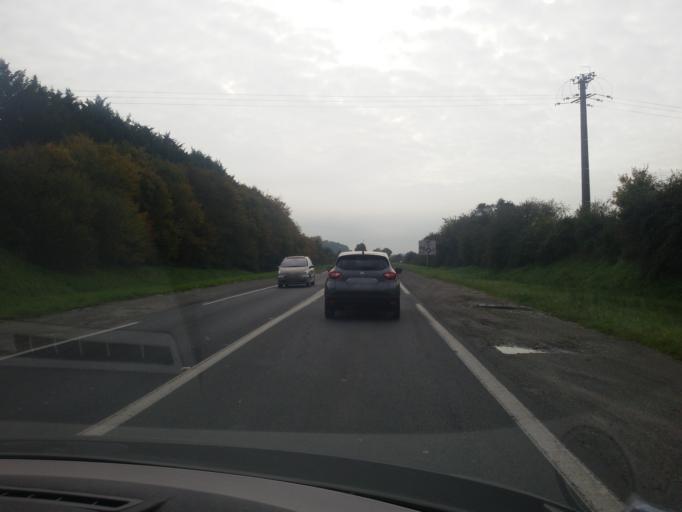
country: FR
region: Lower Normandy
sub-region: Departement du Calvados
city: Dives-sur-Mer
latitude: 49.2613
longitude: -0.1042
